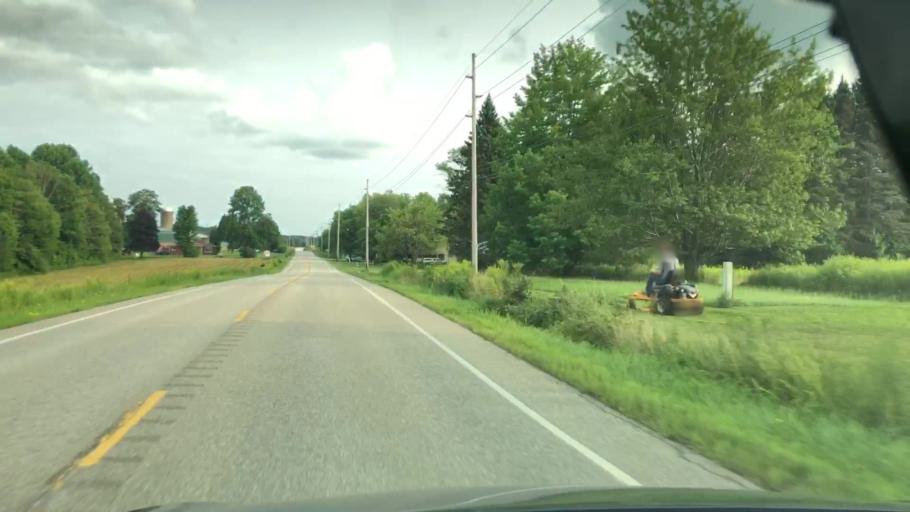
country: US
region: Pennsylvania
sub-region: Erie County
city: Union City
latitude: 41.9521
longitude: -79.8505
